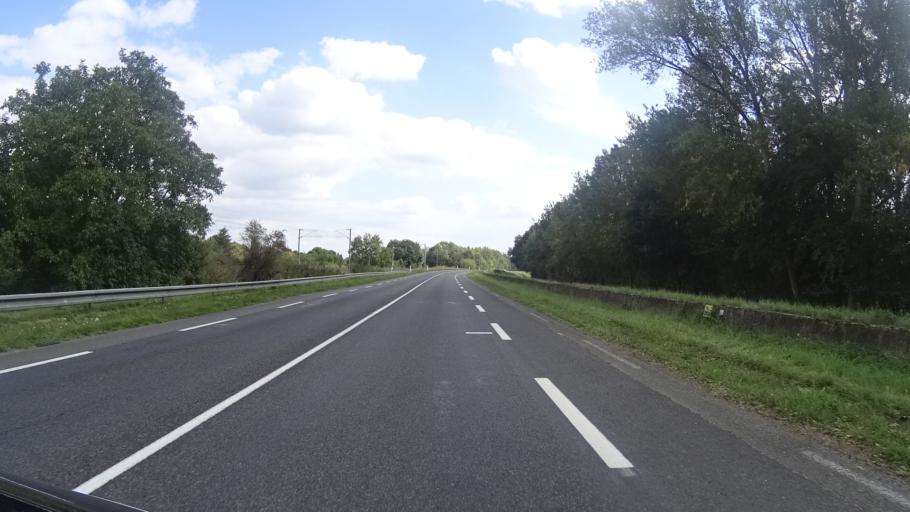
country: FR
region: Pays de la Loire
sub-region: Departement de Maine-et-Loire
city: Saint-Martin-de-la-Place
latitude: 47.3040
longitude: -0.1284
